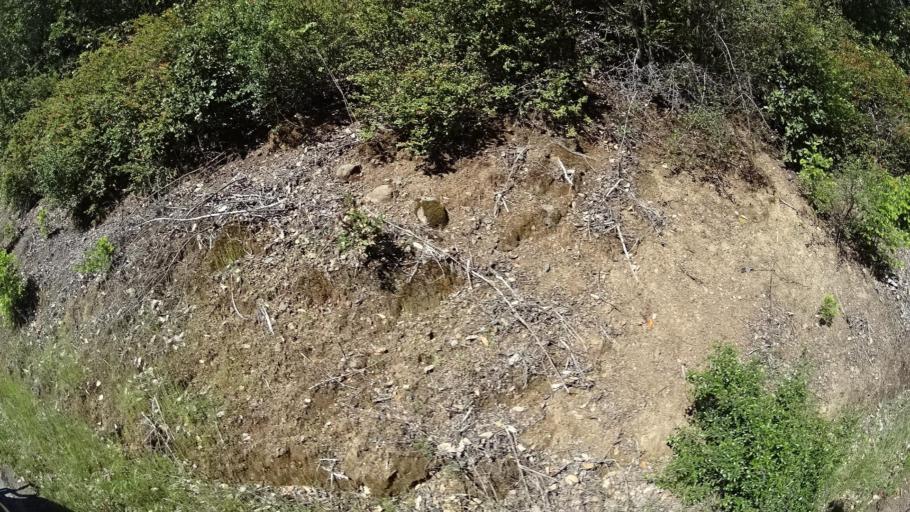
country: US
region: California
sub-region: Humboldt County
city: Rio Dell
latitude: 40.2274
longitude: -124.1095
